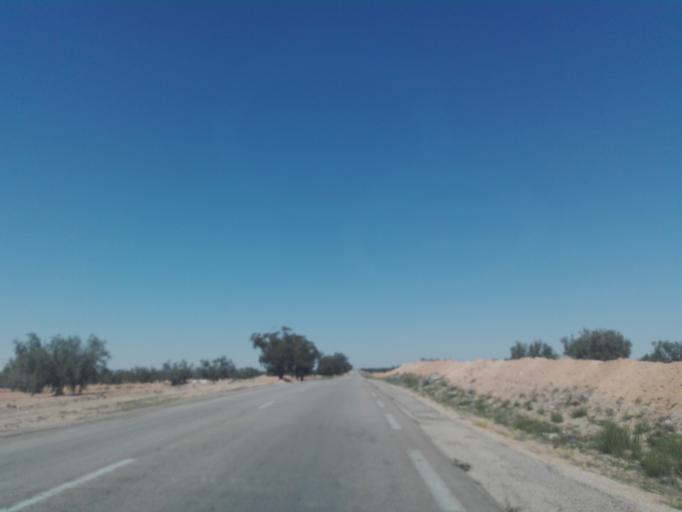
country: TN
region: Safaqis
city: Bi'r `Ali Bin Khalifah
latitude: 34.7573
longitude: 10.3202
